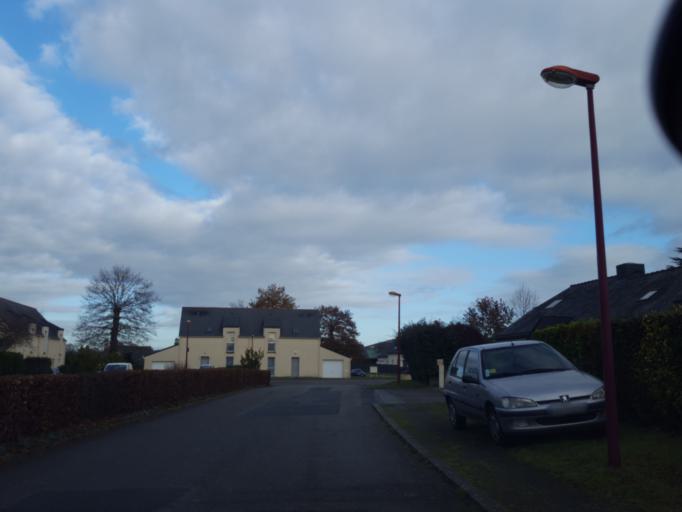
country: FR
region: Brittany
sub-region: Departement d'Ille-et-Vilaine
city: Guignen
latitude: 47.9214
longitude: -1.8652
